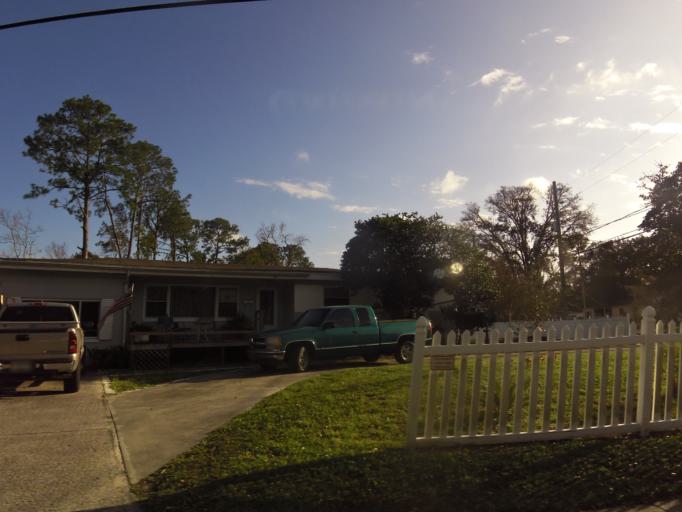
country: US
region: Florida
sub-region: Duval County
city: Jacksonville
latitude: 30.2773
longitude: -81.5989
